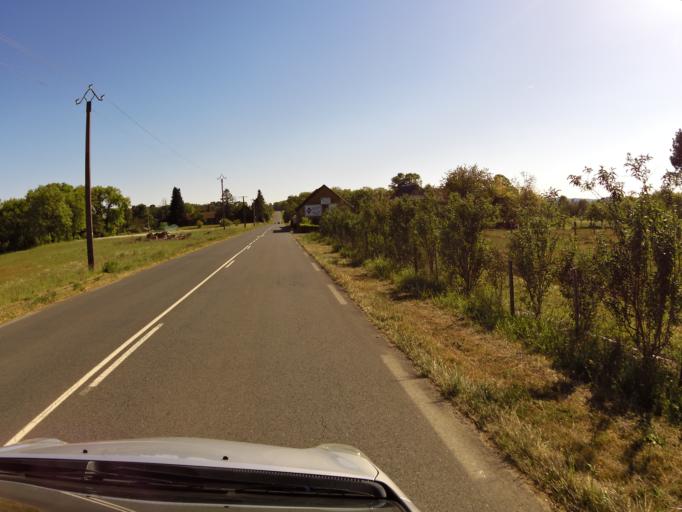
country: FR
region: Aquitaine
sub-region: Departement de la Dordogne
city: Sarlat-la-Caneda
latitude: 44.9895
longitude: 1.2410
